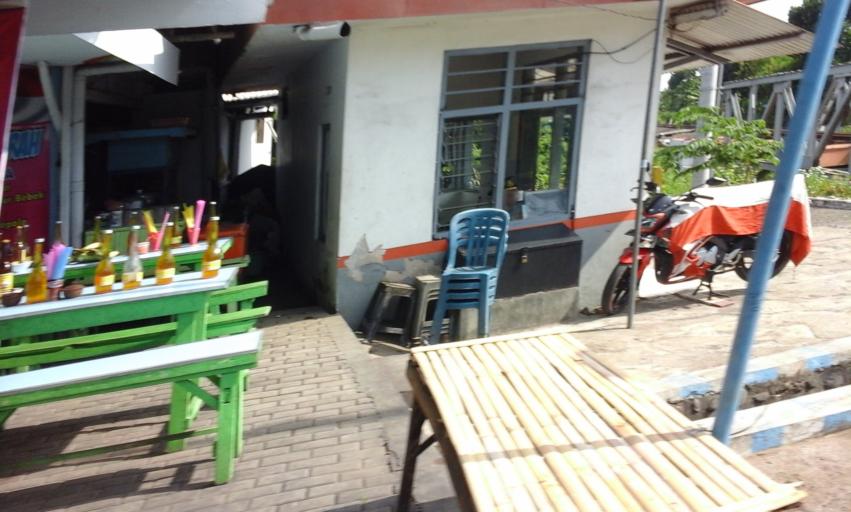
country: ID
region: East Java
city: Krajan
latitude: -8.2142
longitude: 114.3433
